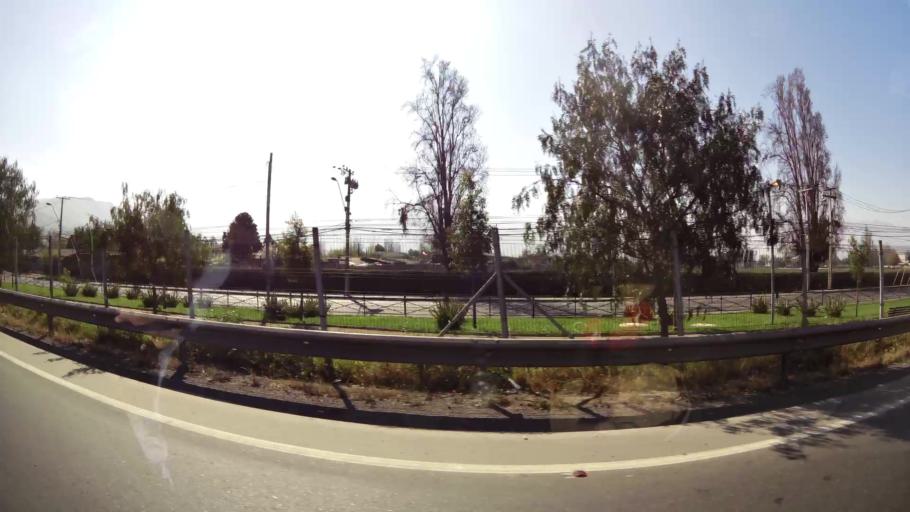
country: CL
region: Santiago Metropolitan
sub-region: Provincia de Chacabuco
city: Chicureo Abajo
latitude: -33.3611
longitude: -70.6902
